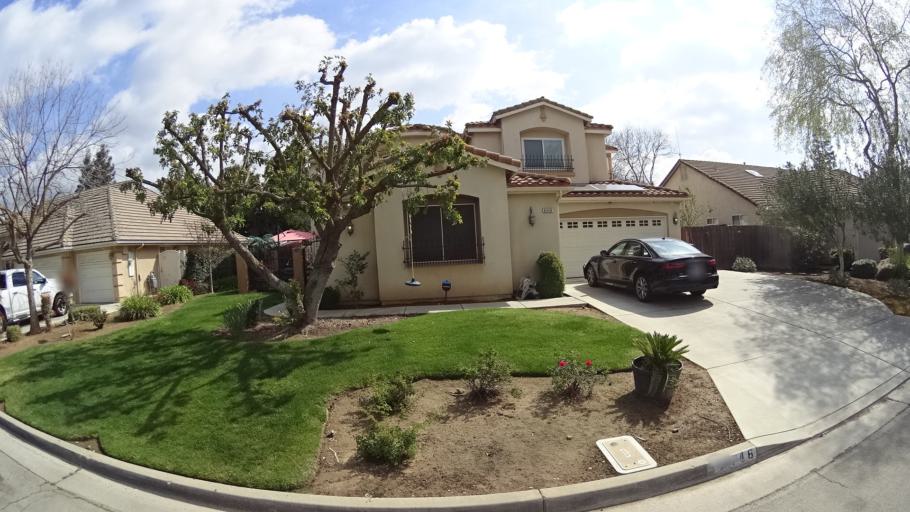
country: US
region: California
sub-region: Fresno County
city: Fresno
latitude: 36.8308
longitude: -119.8564
